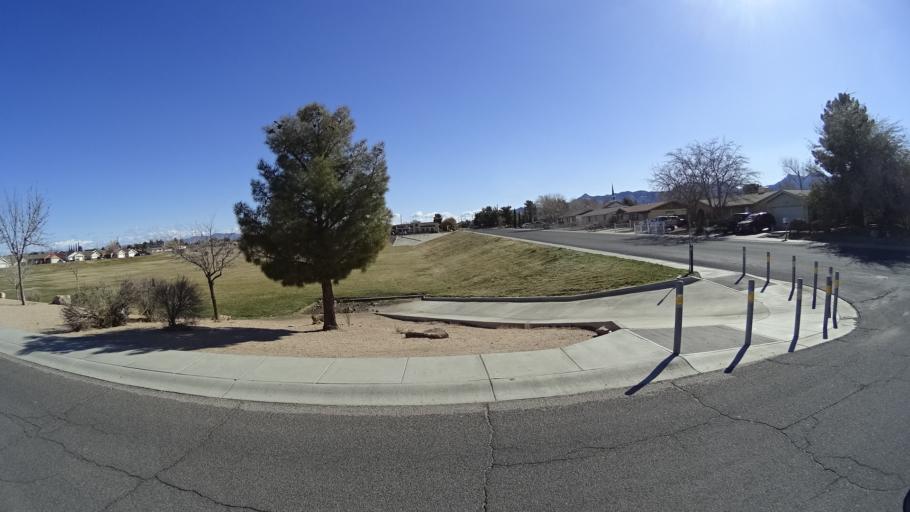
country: US
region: Arizona
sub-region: Mohave County
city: Kingman
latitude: 35.1964
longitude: -114.0139
